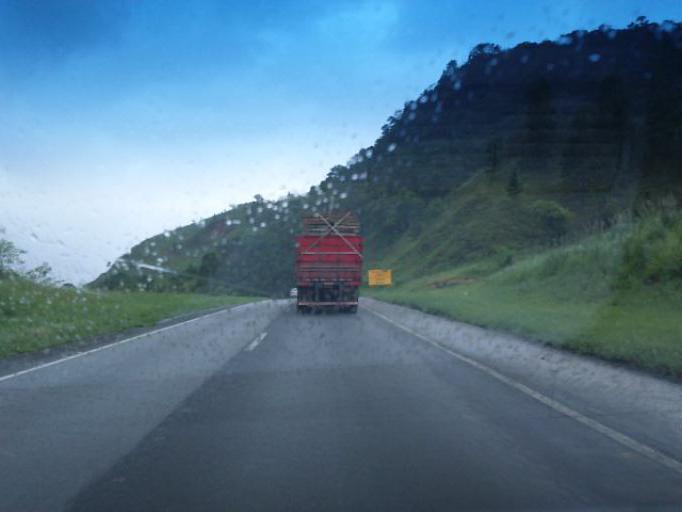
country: BR
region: Sao Paulo
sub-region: Cajati
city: Cajati
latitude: -24.8869
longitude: -48.2260
